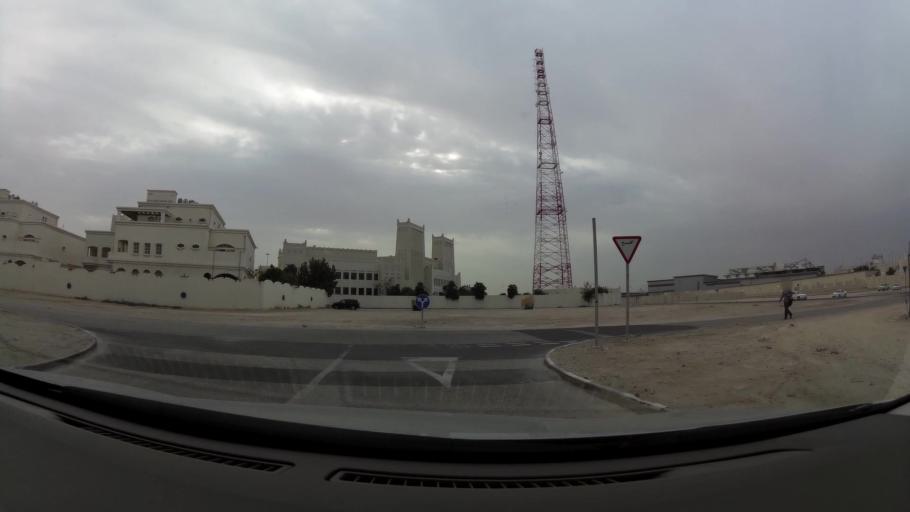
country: QA
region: Baladiyat ad Dawhah
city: Doha
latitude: 25.3099
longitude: 51.5009
